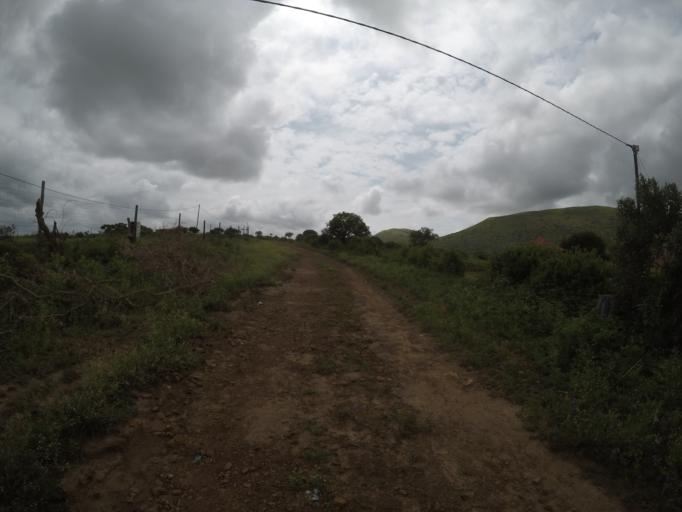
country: ZA
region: KwaZulu-Natal
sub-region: uThungulu District Municipality
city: Empangeni
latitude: -28.5818
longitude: 31.8677
